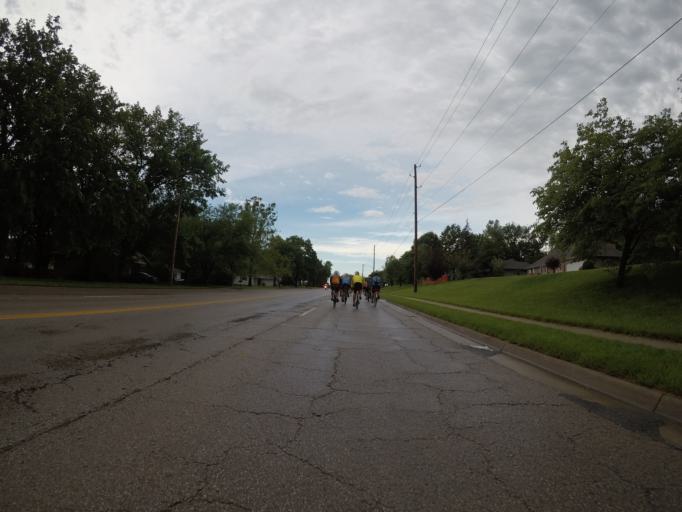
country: US
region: Kansas
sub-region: Shawnee County
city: Topeka
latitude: 39.0117
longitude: -95.6983
